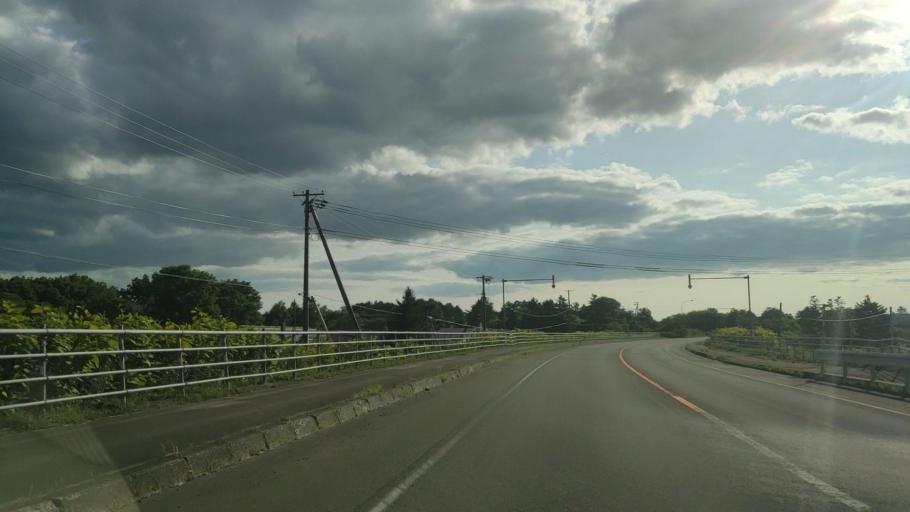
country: JP
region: Hokkaido
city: Makubetsu
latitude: 44.8975
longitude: 141.9287
